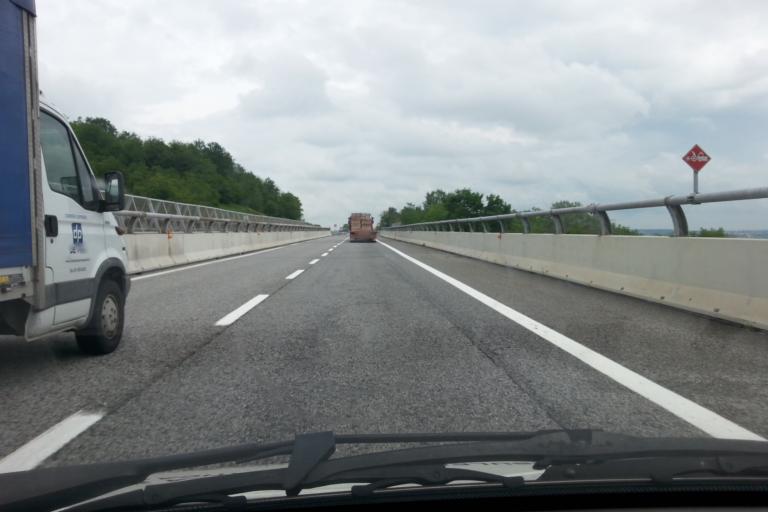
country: IT
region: Piedmont
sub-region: Provincia di Cuneo
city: Bastia Mondovi
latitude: 44.4194
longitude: 7.8911
